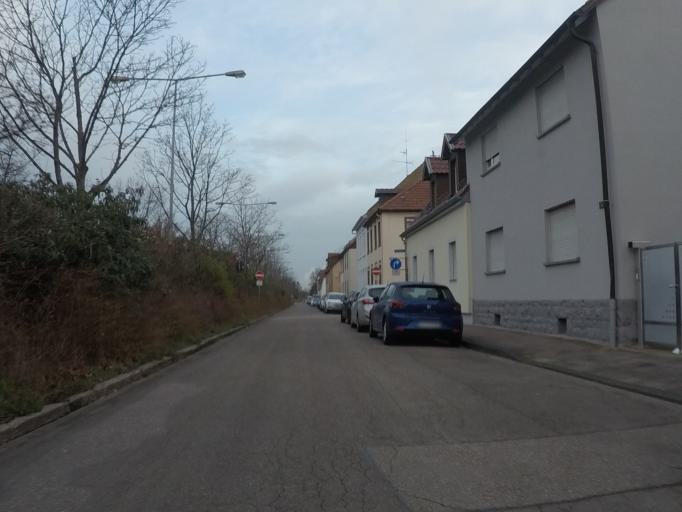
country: DE
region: Baden-Wuerttemberg
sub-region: Karlsruhe Region
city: Karlsruhe
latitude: 49.0320
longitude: 8.3400
